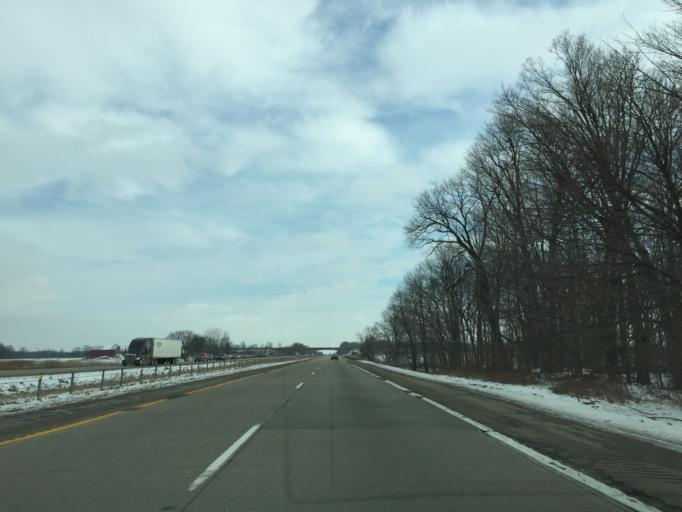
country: US
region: Michigan
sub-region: Kent County
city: Lowell
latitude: 42.8783
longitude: -85.4180
